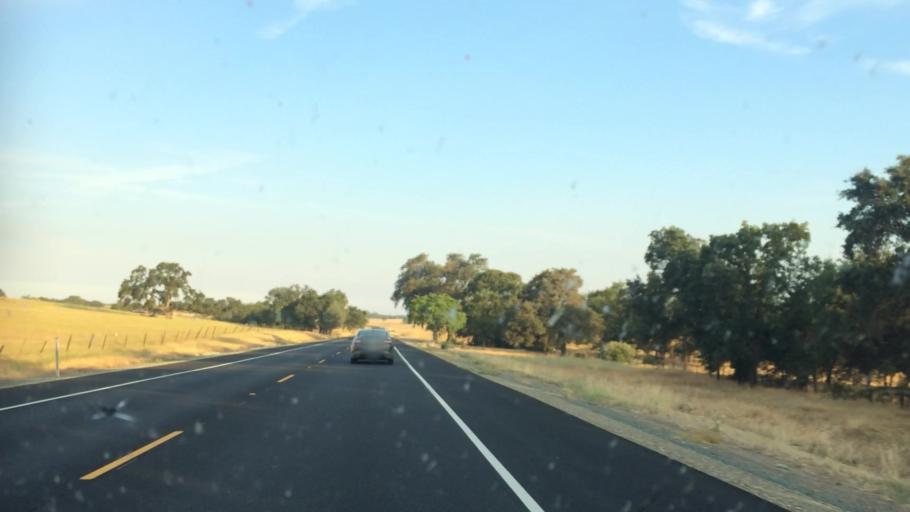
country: US
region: California
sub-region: Amador County
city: Plymouth
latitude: 38.4597
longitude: -120.9321
